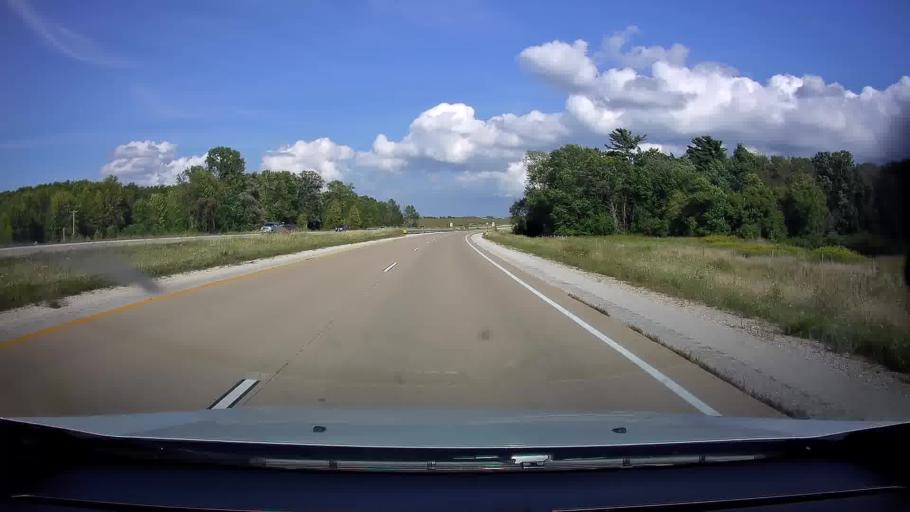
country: US
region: Wisconsin
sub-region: Kewaunee County
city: Luxemburg
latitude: 44.7163
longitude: -87.6779
